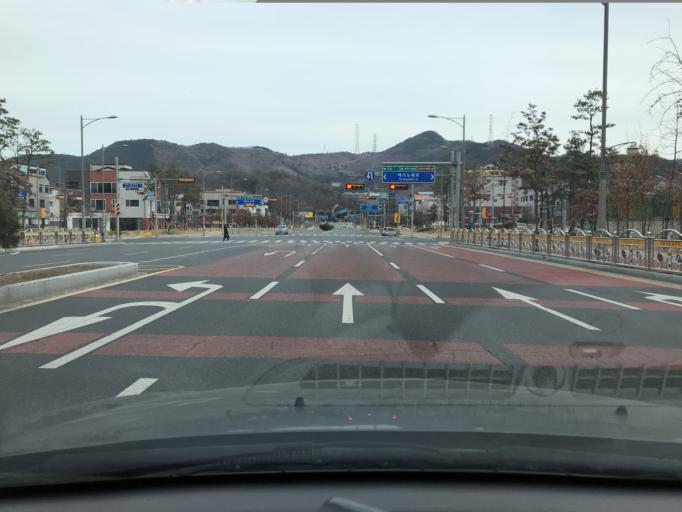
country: KR
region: Daegu
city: Hwawon
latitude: 35.6962
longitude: 128.4579
